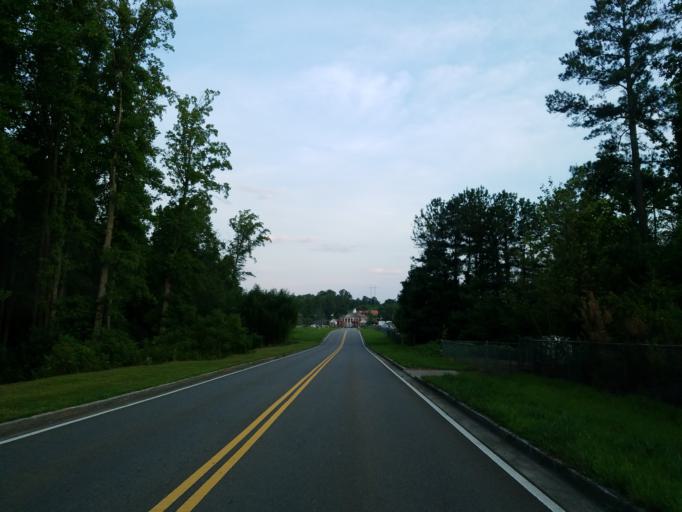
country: US
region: Georgia
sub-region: Pickens County
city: Jasper
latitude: 34.4686
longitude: -84.4522
